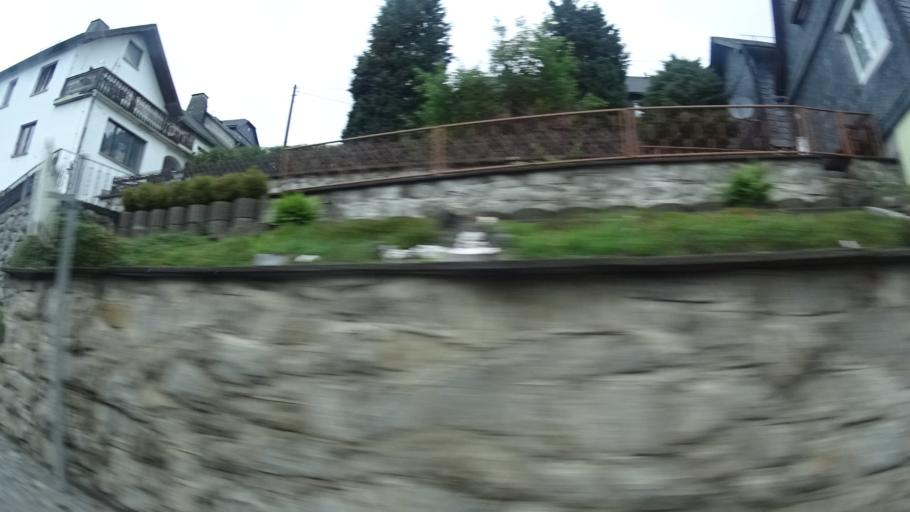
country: DE
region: Thuringia
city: Wurzbach
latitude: 50.4649
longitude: 11.5401
